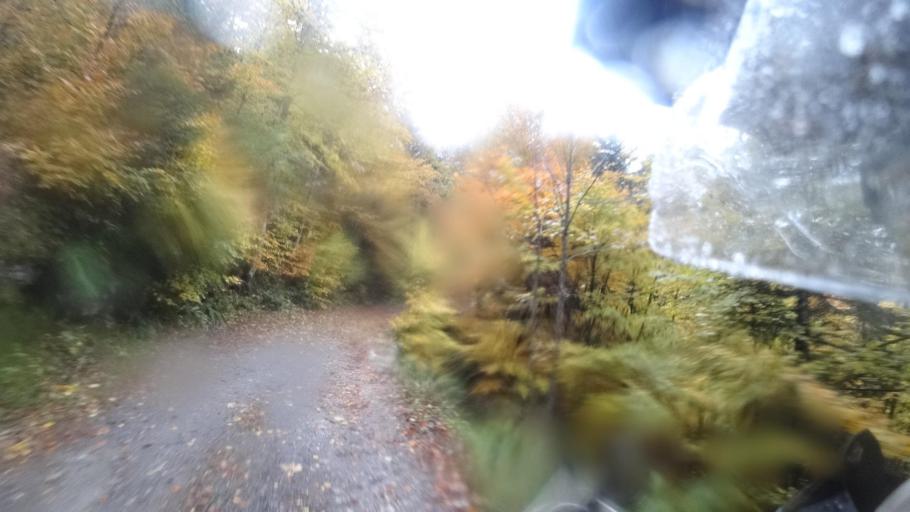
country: HR
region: Primorsko-Goranska
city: Vrbovsko
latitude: 45.3319
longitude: 15.0713
